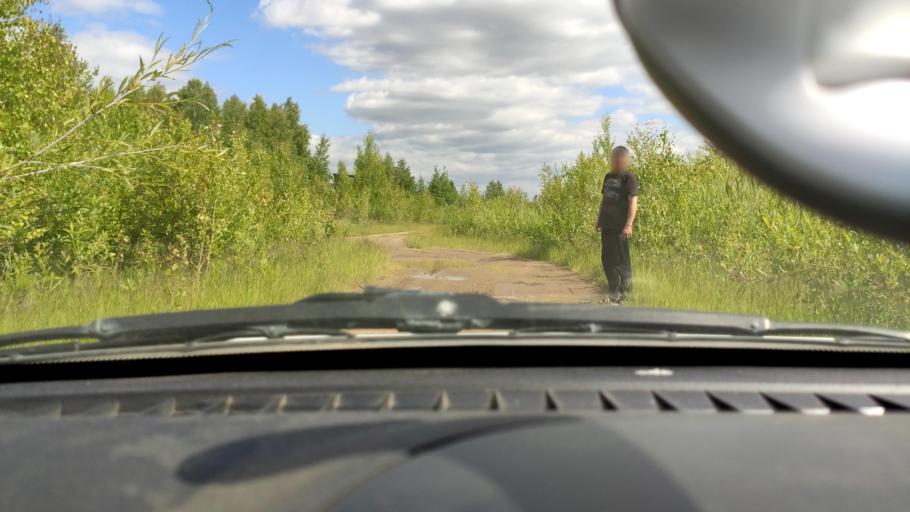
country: RU
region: Perm
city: Kondratovo
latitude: 58.0228
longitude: 56.0717
